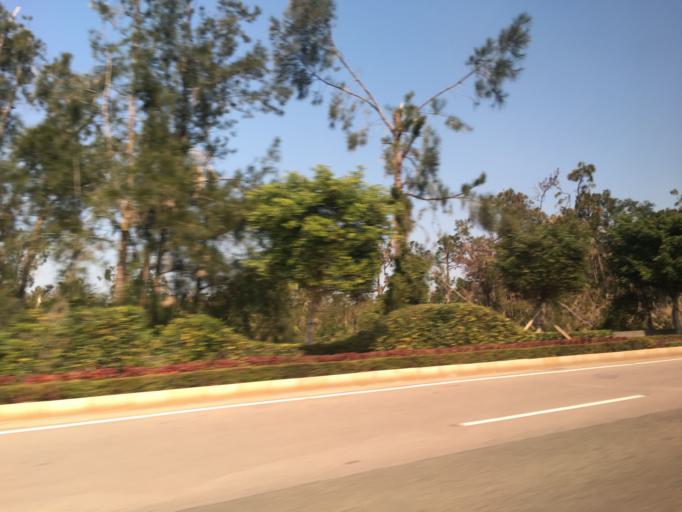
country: TW
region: Fukien
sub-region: Kinmen
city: Jincheng
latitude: 24.4348
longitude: 118.3490
